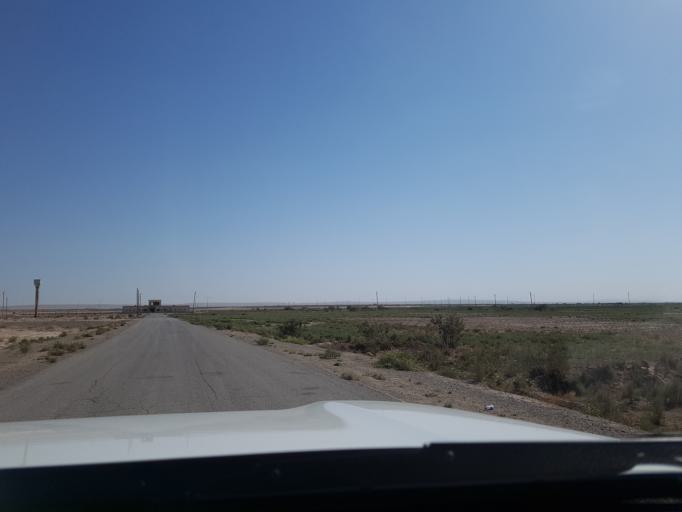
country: IR
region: Razavi Khorasan
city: Sarakhs
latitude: 36.4944
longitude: 61.2540
